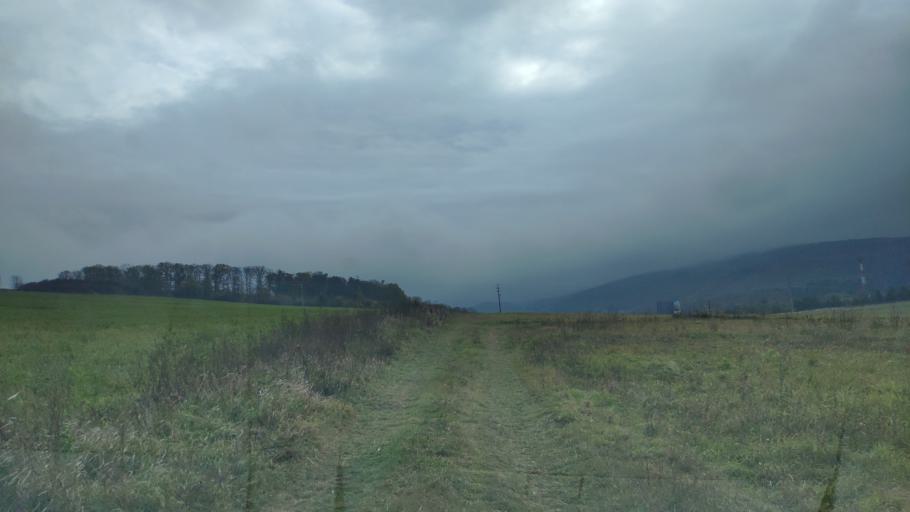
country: SK
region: Presovsky
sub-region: Okres Presov
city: Presov
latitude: 49.0060
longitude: 21.1937
